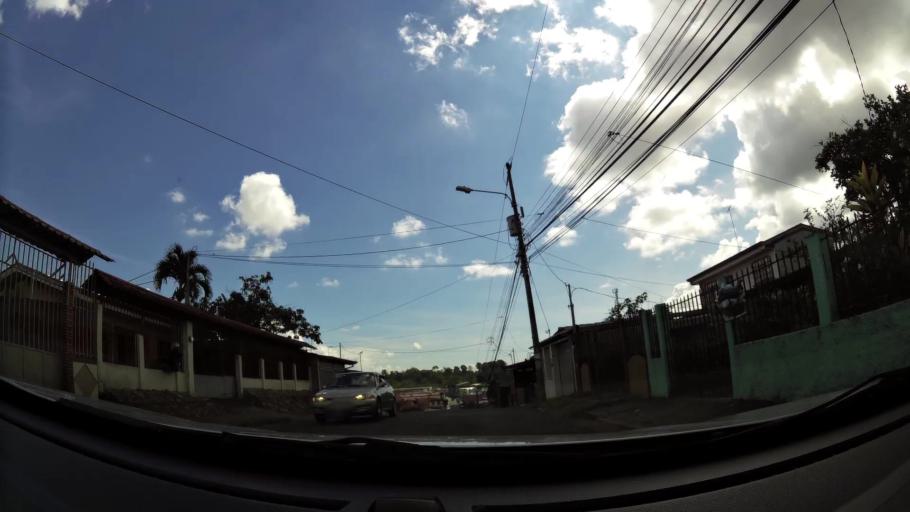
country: CR
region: San Jose
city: San Isidro
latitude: 9.3710
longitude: -83.7075
